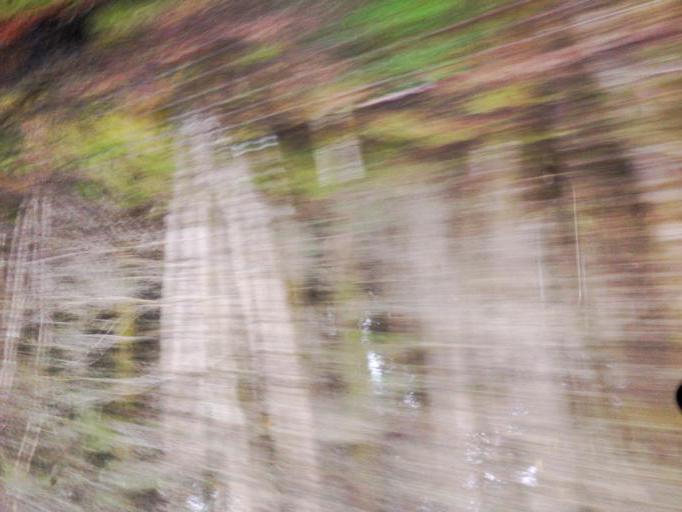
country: GB
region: Scotland
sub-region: Highland
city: Fort William
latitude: 56.8458
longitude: -5.1568
